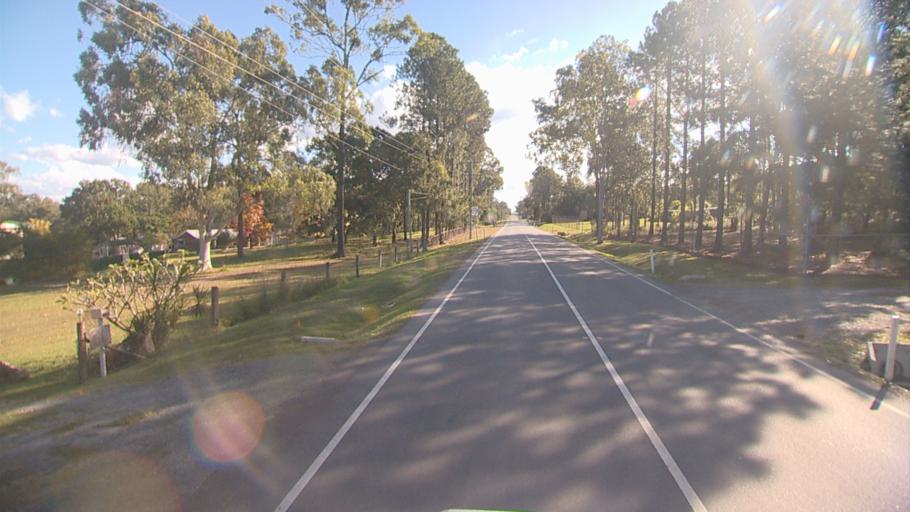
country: AU
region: Queensland
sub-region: Logan
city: Park Ridge South
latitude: -27.7106
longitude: 153.0279
